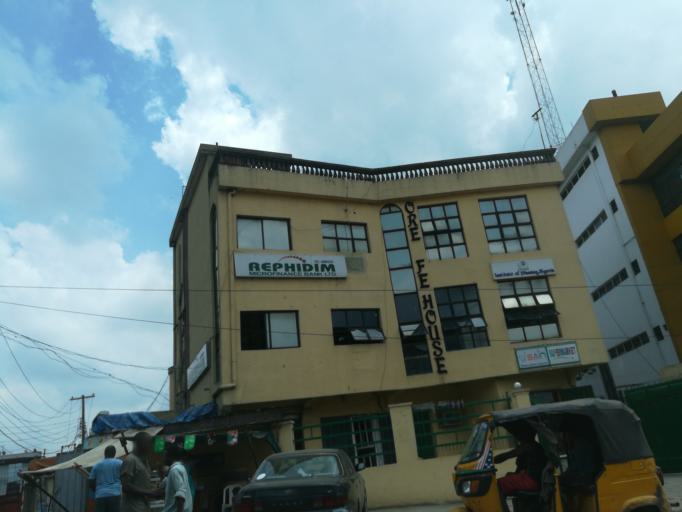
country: NG
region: Lagos
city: Oshodi
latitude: 6.5461
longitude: 3.3328
